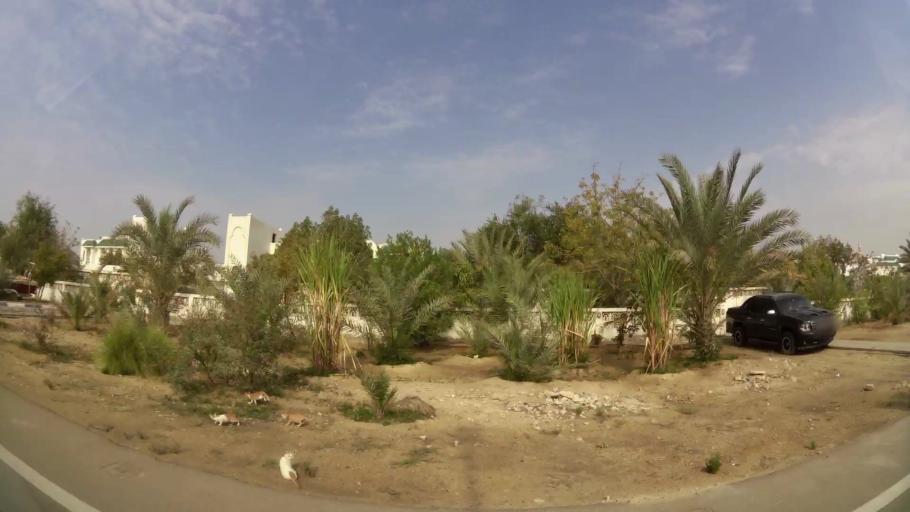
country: AE
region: Abu Dhabi
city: Abu Dhabi
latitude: 24.6611
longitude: 54.7601
